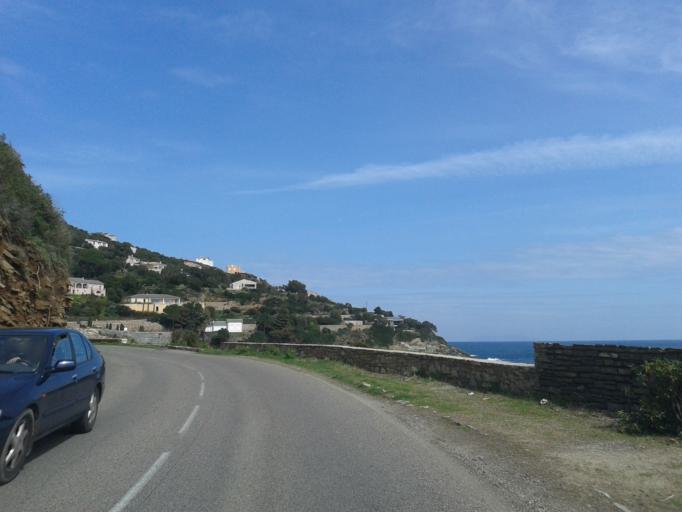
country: FR
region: Corsica
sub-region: Departement de la Haute-Corse
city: Brando
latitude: 42.7785
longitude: 9.4787
